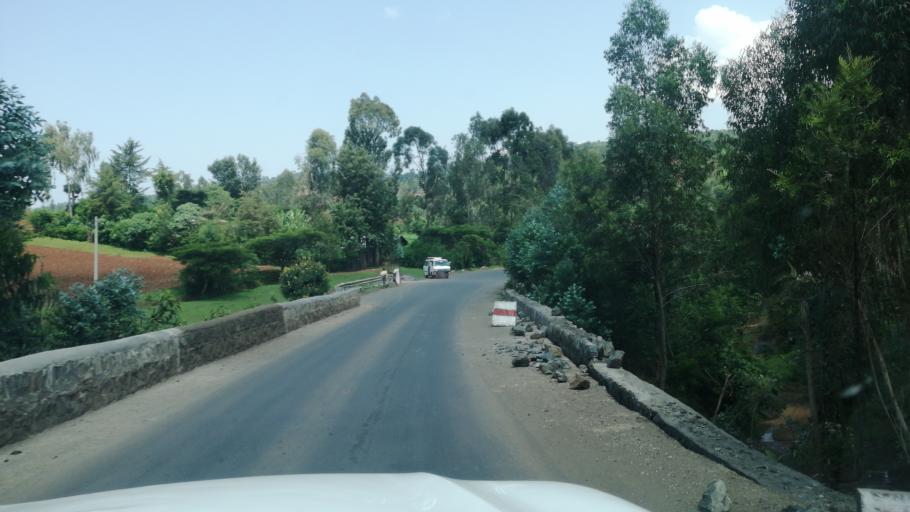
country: ET
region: Oromiya
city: Gedo
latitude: 8.9735
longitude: 37.5566
